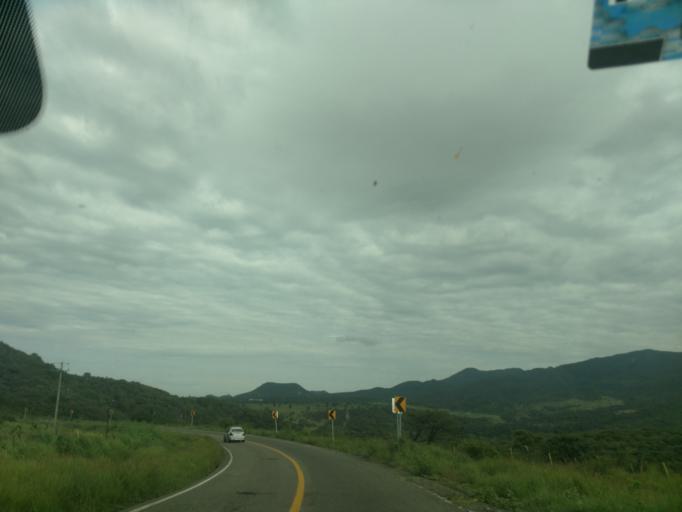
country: MX
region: Jalisco
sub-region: Atengo
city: Soyatlan del Oro
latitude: 20.5494
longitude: -104.2998
